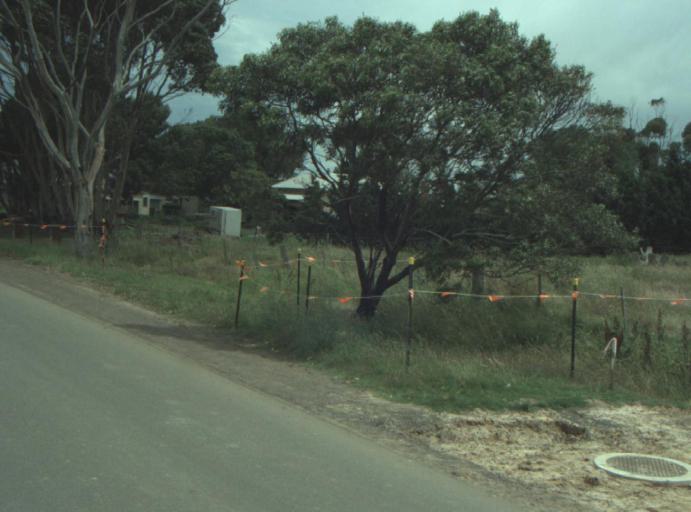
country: AU
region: Victoria
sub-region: Greater Geelong
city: Leopold
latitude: -38.1976
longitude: 144.4534
